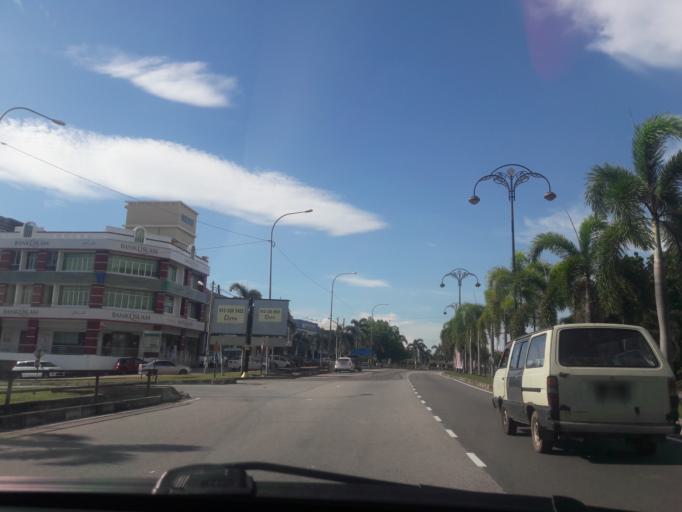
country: MY
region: Kedah
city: Sungai Petani
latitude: 5.6165
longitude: 100.4728
